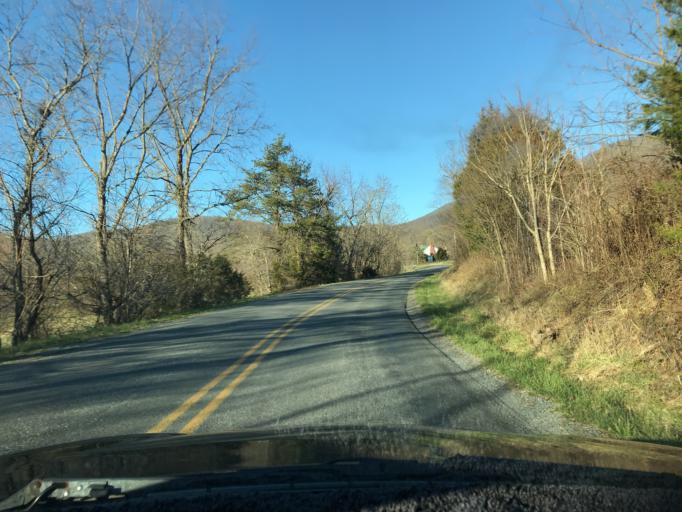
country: US
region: Virginia
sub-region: Botetourt County
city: Buchanan
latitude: 37.4550
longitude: -79.6643
